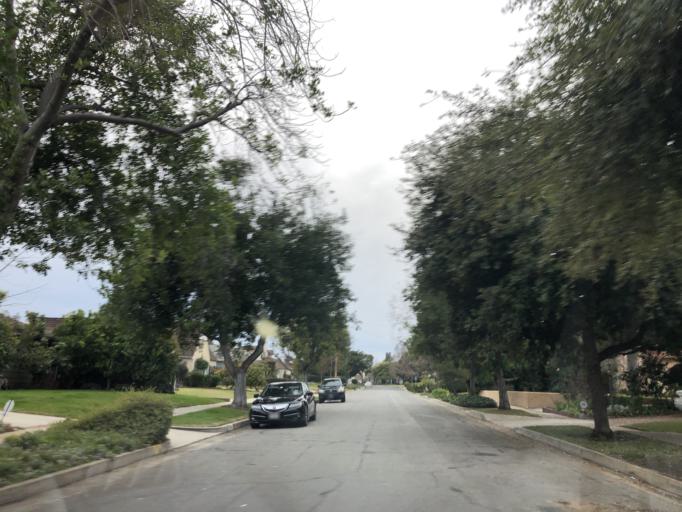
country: US
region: California
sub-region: Los Angeles County
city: San Marino
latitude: 34.1158
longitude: -118.0925
